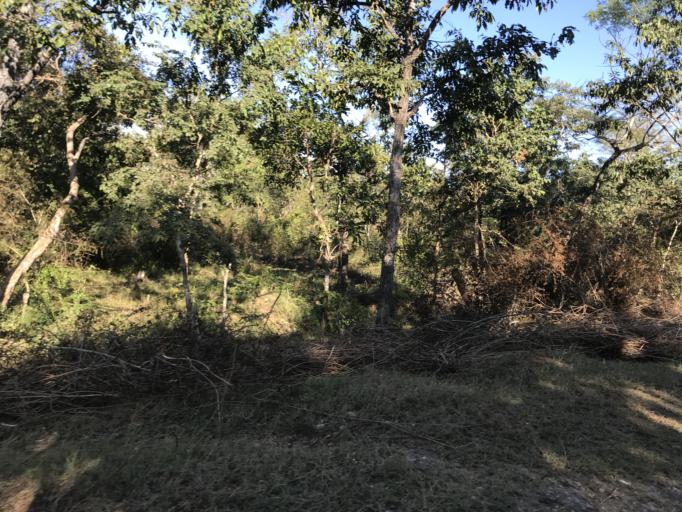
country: IN
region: Karnataka
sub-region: Mysore
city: Heggadadevankote
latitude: 11.9781
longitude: 76.2386
